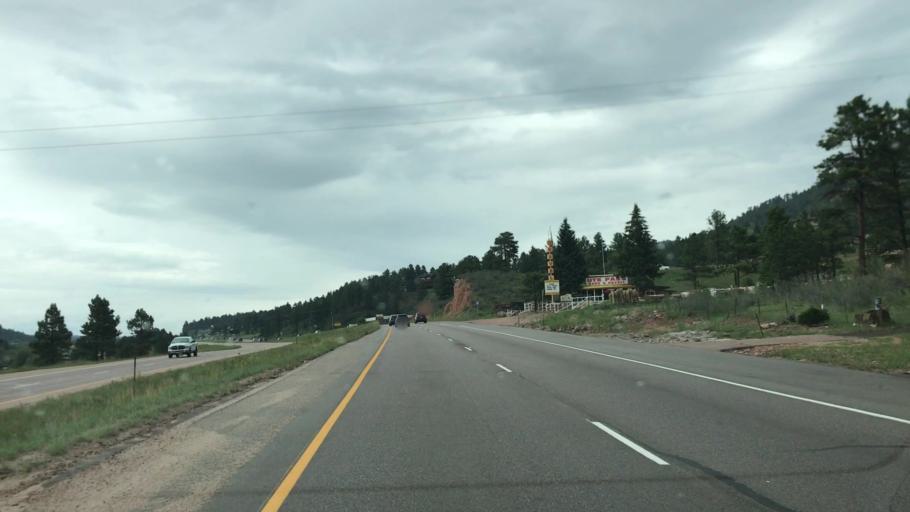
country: US
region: Colorado
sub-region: El Paso County
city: Cascade-Chipita Park
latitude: 38.9600
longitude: -105.0288
